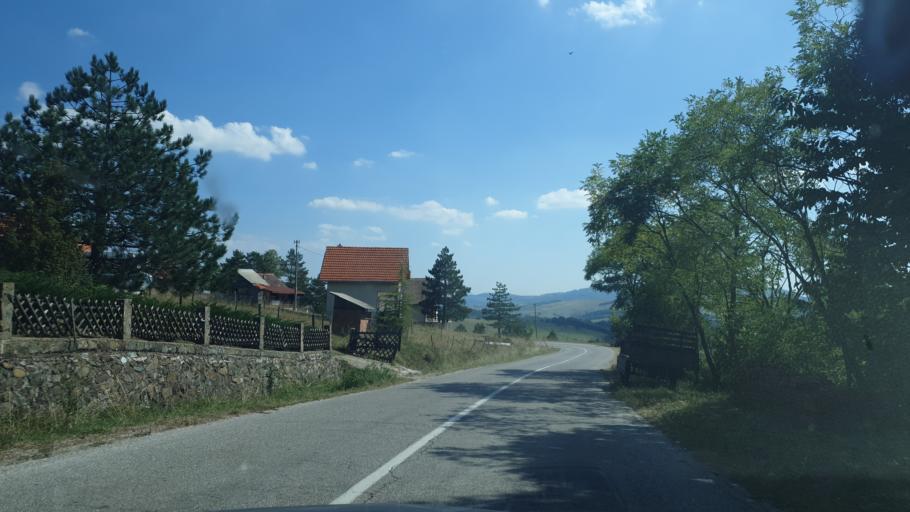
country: RS
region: Central Serbia
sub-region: Zlatiborski Okrug
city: Kosjeric
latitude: 44.0778
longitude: 20.0212
